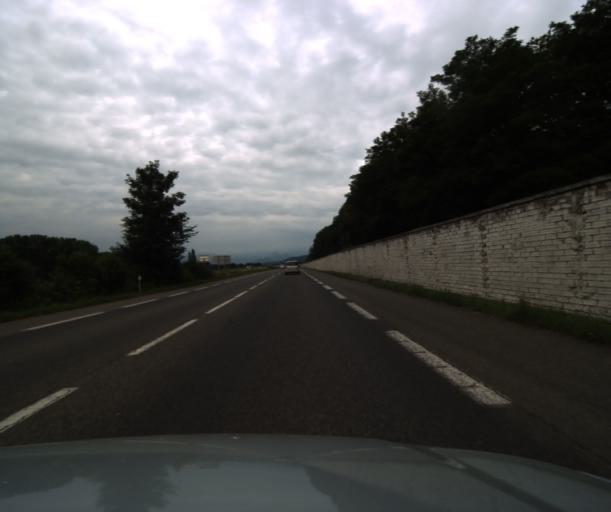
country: FR
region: Midi-Pyrenees
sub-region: Departement des Hautes-Pyrenees
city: Juillan
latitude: 43.1777
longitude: 0.0062
